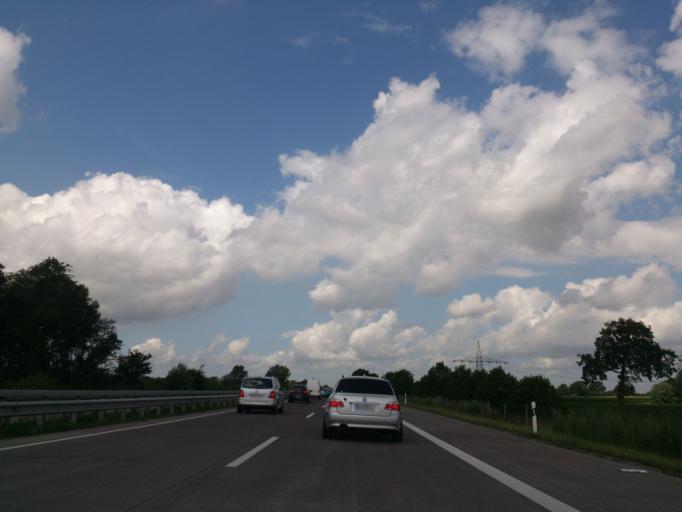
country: DE
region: Schleswig-Holstein
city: Hohenfelde
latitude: 53.8362
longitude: 9.6168
